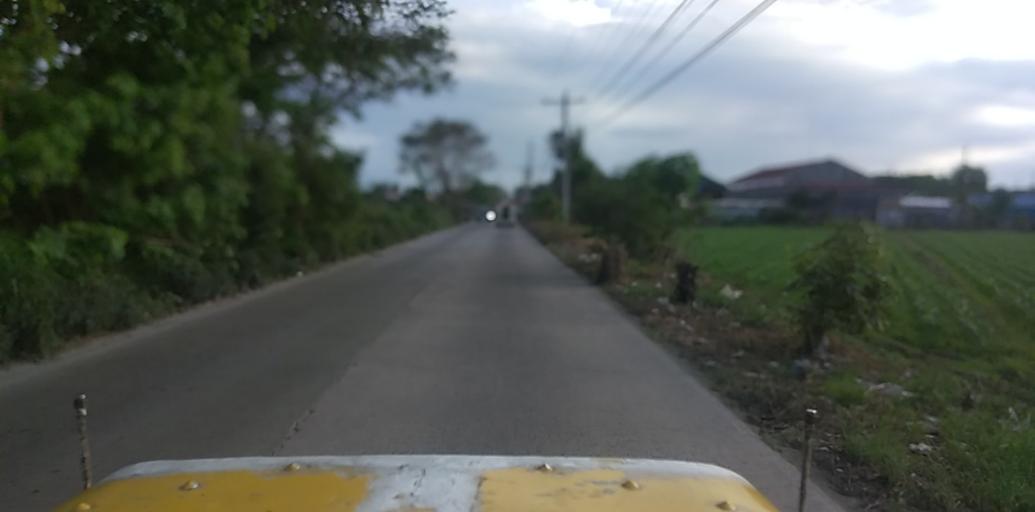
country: PH
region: Central Luzon
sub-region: Province of Pampanga
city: San Antonio
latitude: 15.1486
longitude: 120.6901
